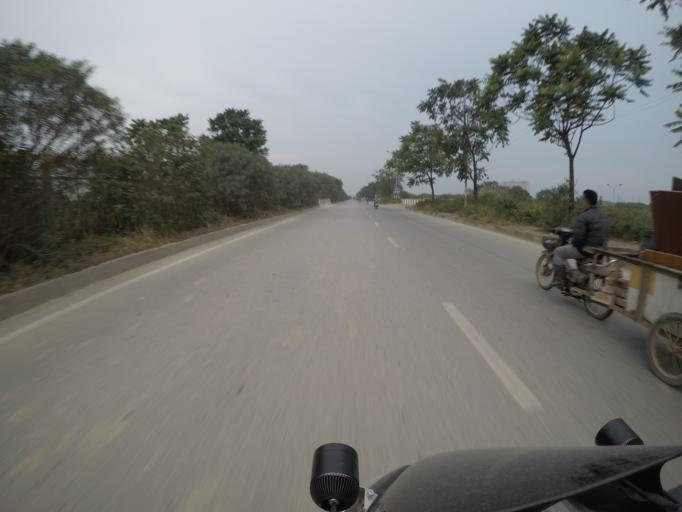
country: VN
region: Ha Noi
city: Cau Dien
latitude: 21.0080
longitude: 105.7572
